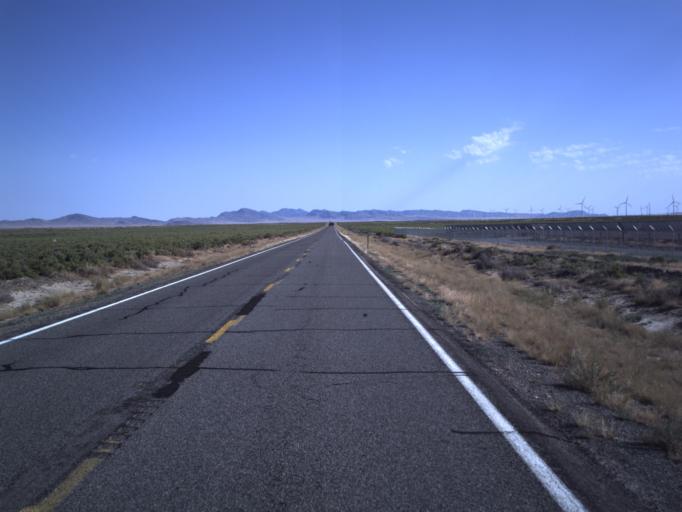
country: US
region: Utah
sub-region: Beaver County
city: Milford
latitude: 38.5120
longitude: -112.9911
